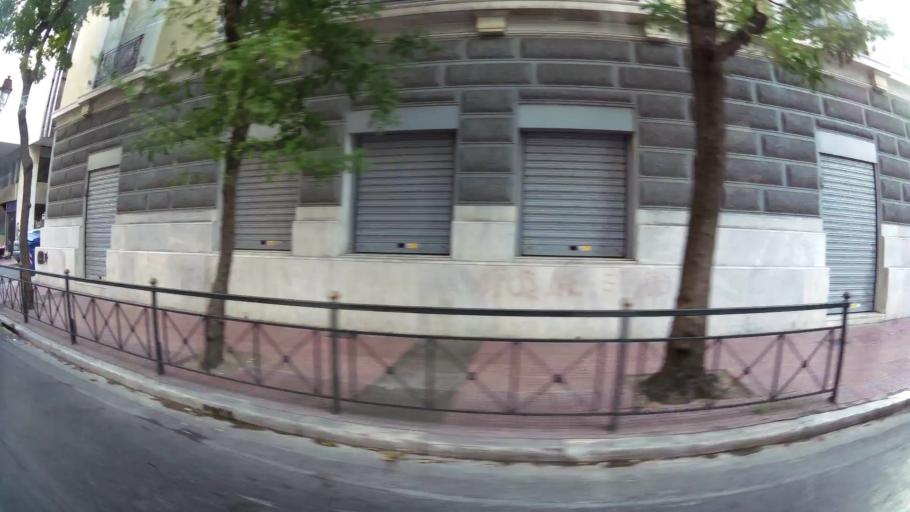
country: GR
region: Attica
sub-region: Nomarchia Athinas
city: Athens
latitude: 37.9773
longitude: 23.7377
